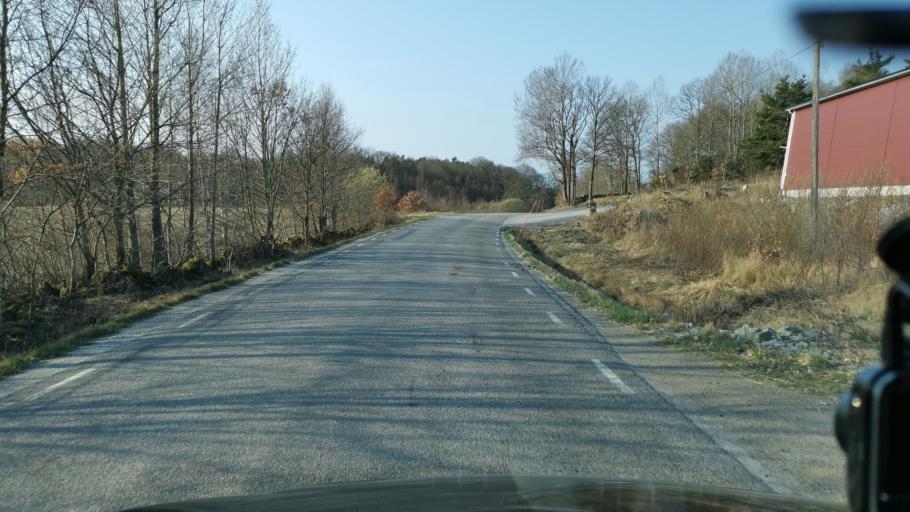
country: SE
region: Vaestra Goetaland
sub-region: Kungalvs Kommun
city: Kode
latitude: 57.9702
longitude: 11.8262
